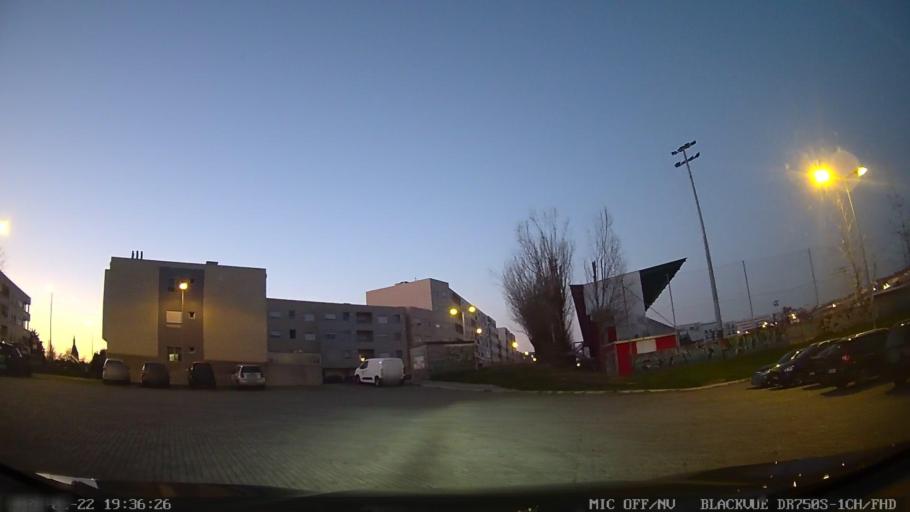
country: PT
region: Porto
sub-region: Matosinhos
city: Senhora da Hora
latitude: 41.1857
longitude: -8.6352
